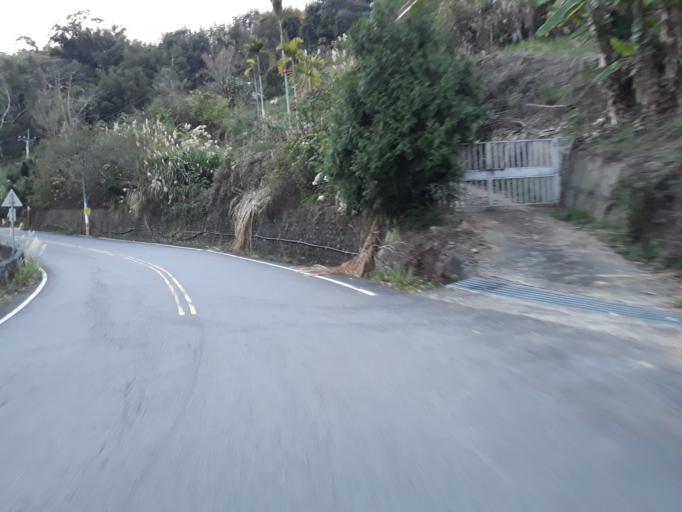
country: TW
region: Taiwan
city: Fengyuan
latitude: 24.3671
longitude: 120.8677
